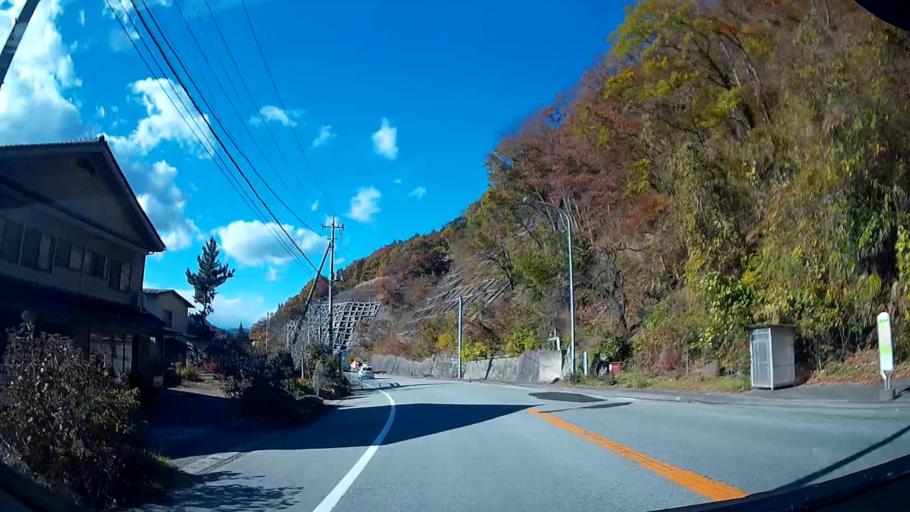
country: JP
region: Yamanashi
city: Enzan
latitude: 35.6475
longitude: 138.7631
